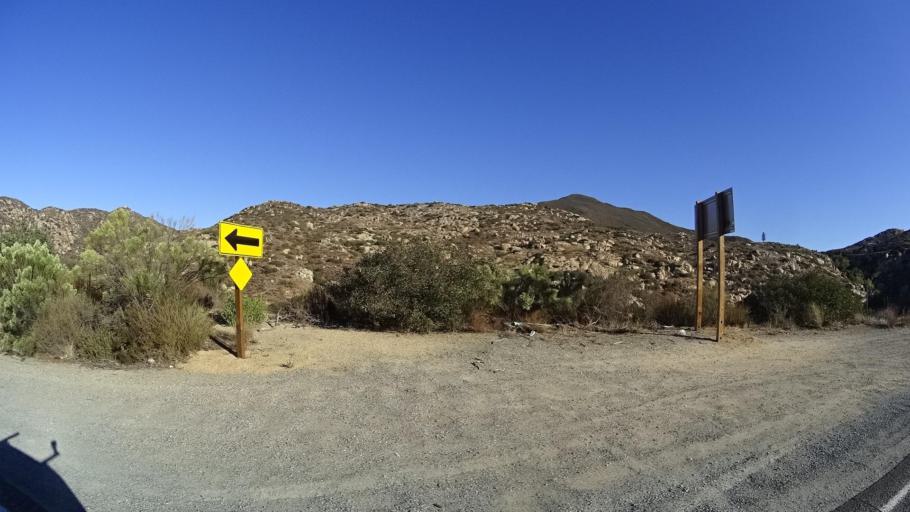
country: MX
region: Baja California
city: Tecate
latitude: 32.6020
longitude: -116.6381
